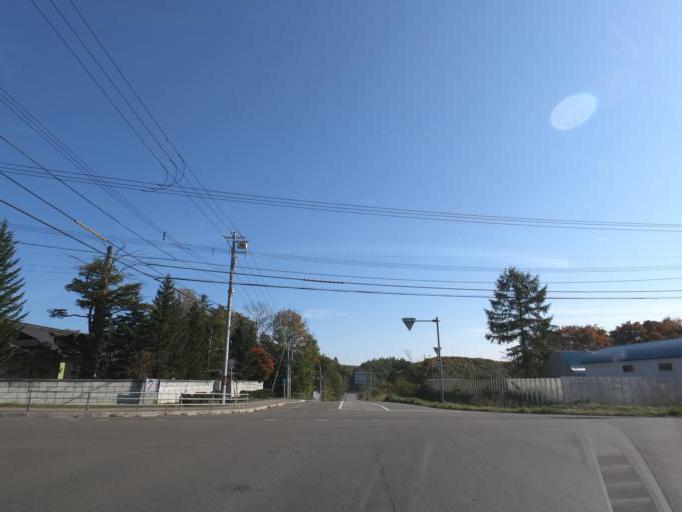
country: JP
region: Hokkaido
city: Otofuke
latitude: 42.9604
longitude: 143.2503
